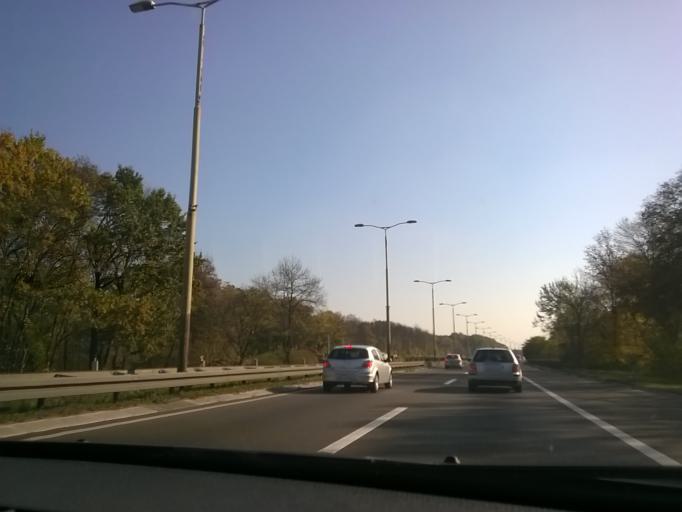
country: RS
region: Central Serbia
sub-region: Belgrade
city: Zemun
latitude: 44.8300
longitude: 20.3781
